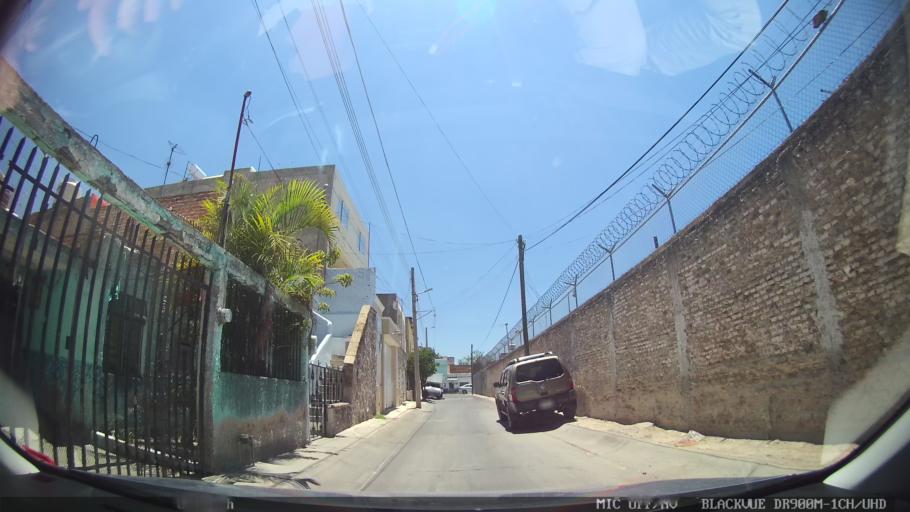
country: MX
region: Jalisco
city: Tlaquepaque
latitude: 20.6541
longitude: -103.2765
